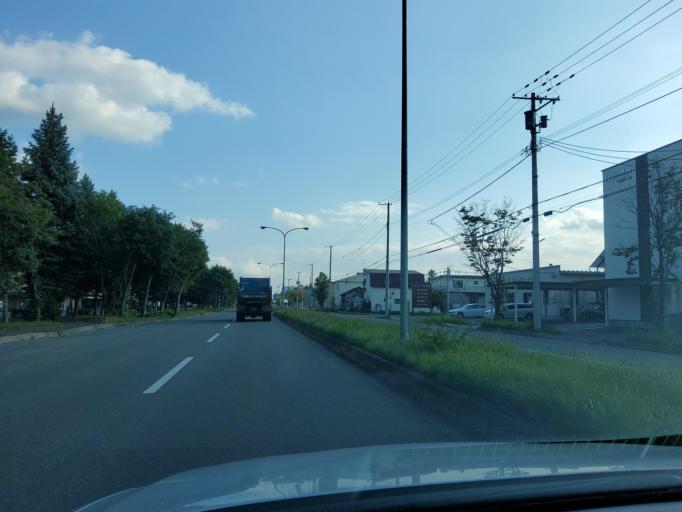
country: JP
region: Hokkaido
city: Obihiro
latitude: 42.9075
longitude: 143.2137
